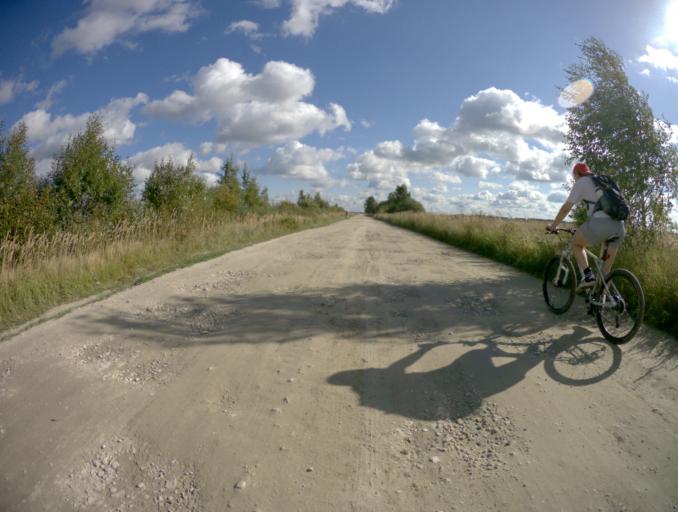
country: RU
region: Vladimir
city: Lakinsk
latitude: 55.9135
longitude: 39.8410
